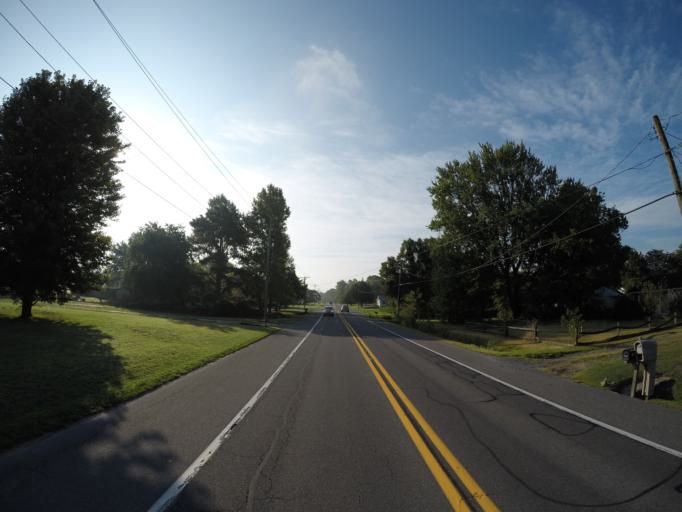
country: US
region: Delaware
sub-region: Sussex County
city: Selbyville
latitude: 38.5368
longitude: -75.2164
